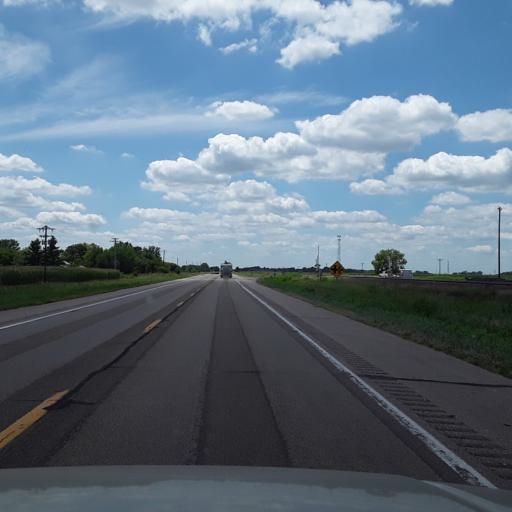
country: US
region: Nebraska
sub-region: Nance County
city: Genoa
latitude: 41.3281
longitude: -97.6347
